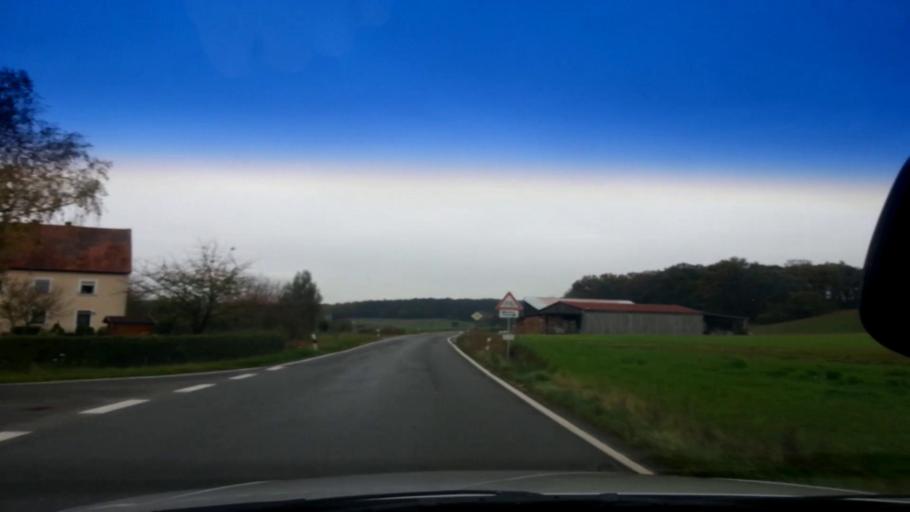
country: DE
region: Bavaria
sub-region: Upper Franconia
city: Burgebrach
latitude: 49.8228
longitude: 10.7845
